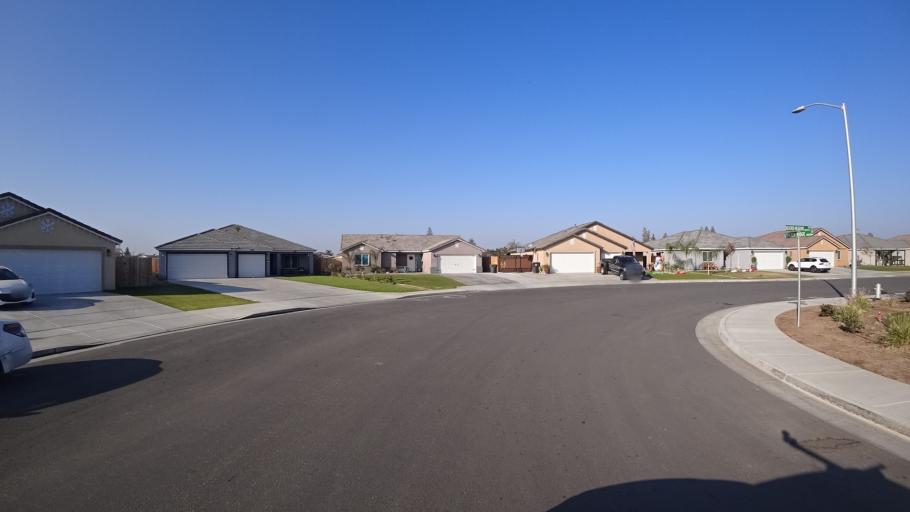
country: US
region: California
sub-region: Kern County
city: Greenfield
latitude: 35.2652
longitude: -119.0143
